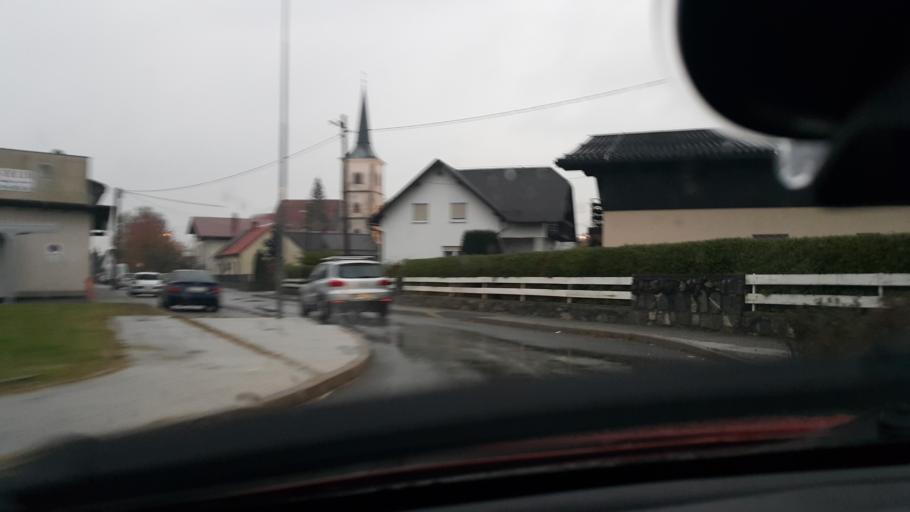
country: SI
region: Miklavz na Dravskem Polju
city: Miklavz na Dravskem Polju
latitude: 46.5372
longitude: 15.6877
